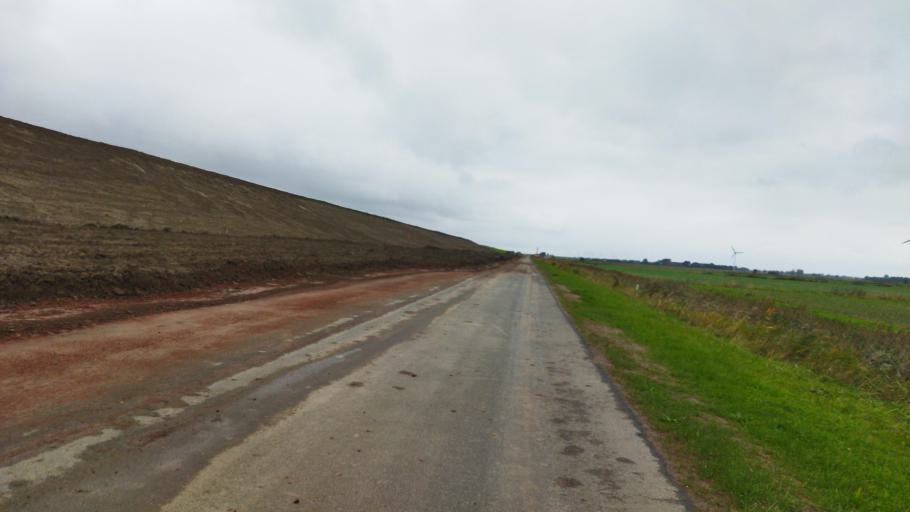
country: NL
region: Groningen
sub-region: Gemeente Delfzijl
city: Delfzijl
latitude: 53.4411
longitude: 7.0196
